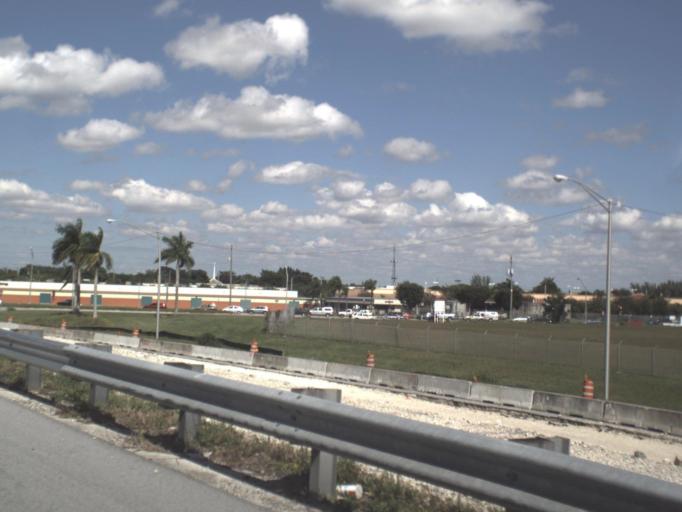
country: US
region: Florida
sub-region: Miami-Dade County
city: South Miami Heights
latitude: 25.5940
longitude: -80.3705
